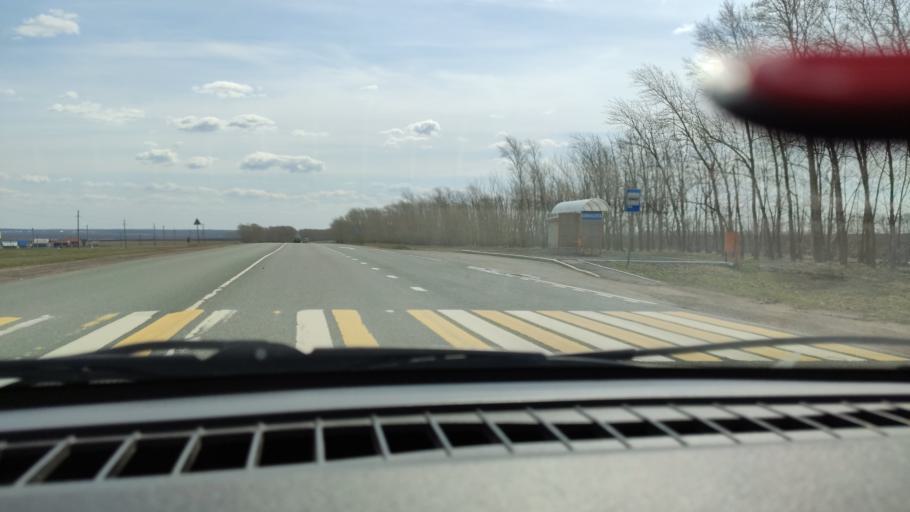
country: RU
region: Bashkortostan
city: Kushnarenkovo
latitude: 55.1915
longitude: 55.1192
